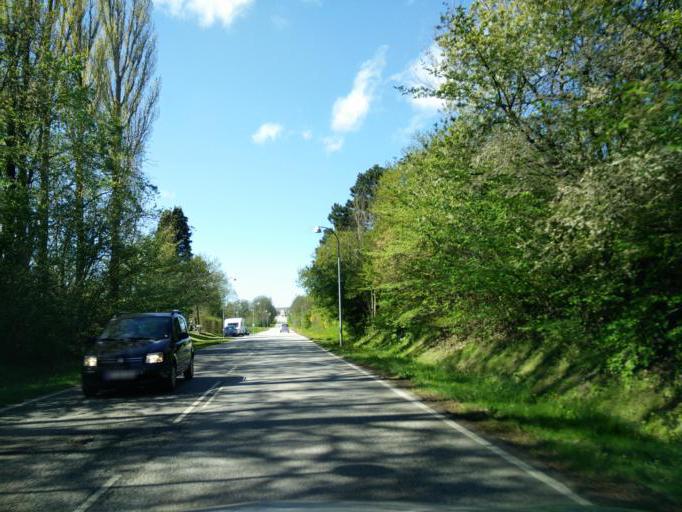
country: DK
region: Capital Region
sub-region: Gribskov Kommune
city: Helsinge
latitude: 56.0131
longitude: 12.2106
